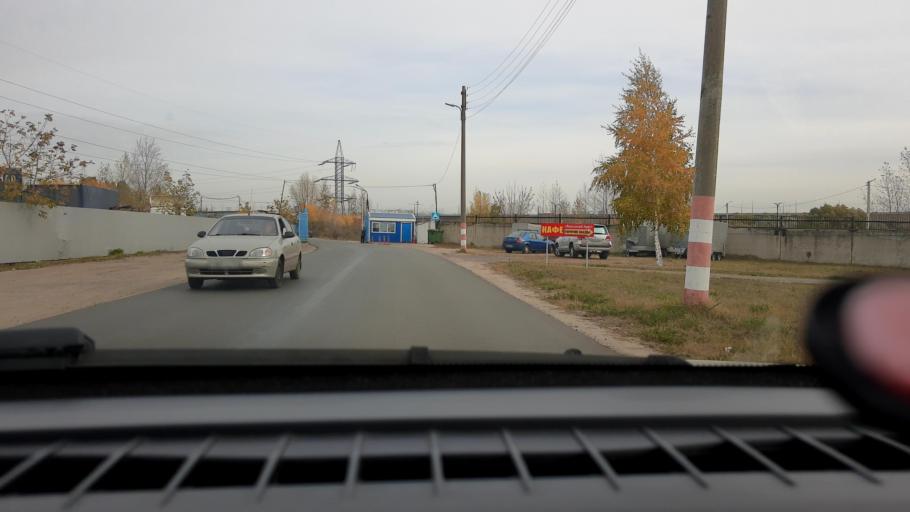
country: RU
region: Nizjnij Novgorod
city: Nizhniy Novgorod
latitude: 56.2496
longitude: 43.9356
